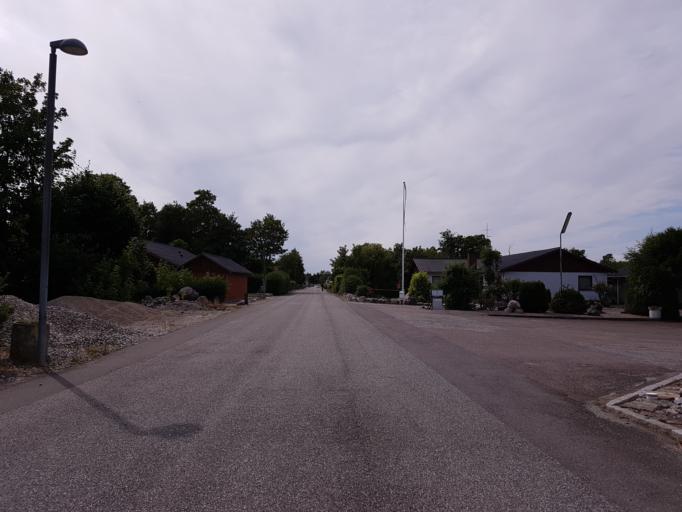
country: DK
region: Zealand
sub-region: Guldborgsund Kommune
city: Nykobing Falster
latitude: 54.5803
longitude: 11.9311
